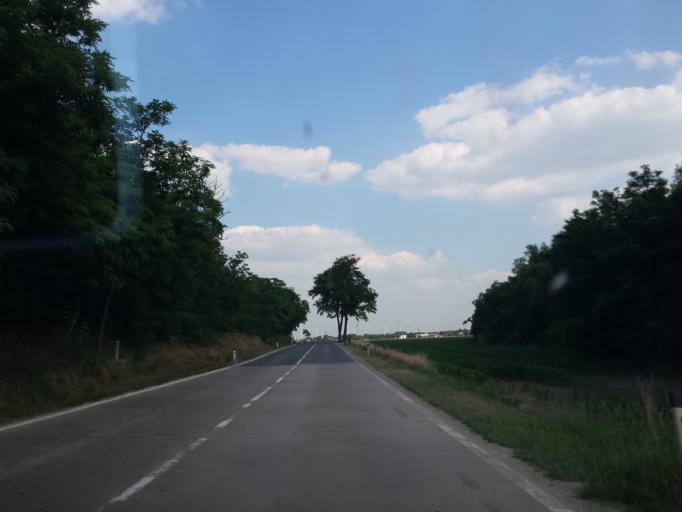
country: AT
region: Lower Austria
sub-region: Politischer Bezirk Ganserndorf
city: Parbasdorf
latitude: 48.2762
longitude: 16.6123
